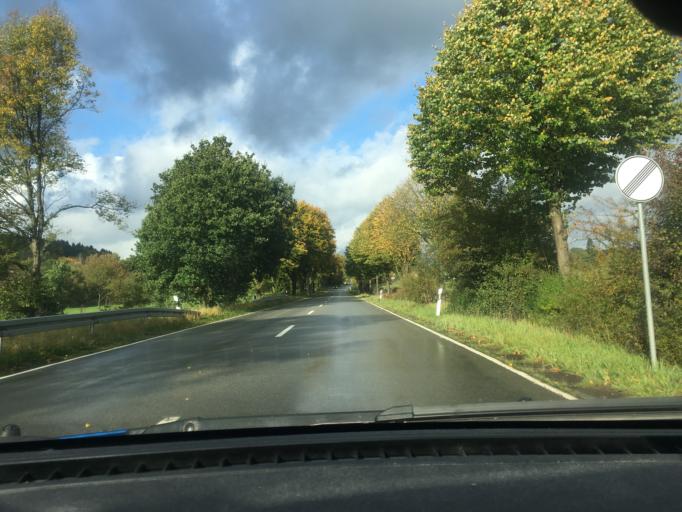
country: DE
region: Lower Saxony
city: Derental
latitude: 51.7449
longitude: 9.5180
